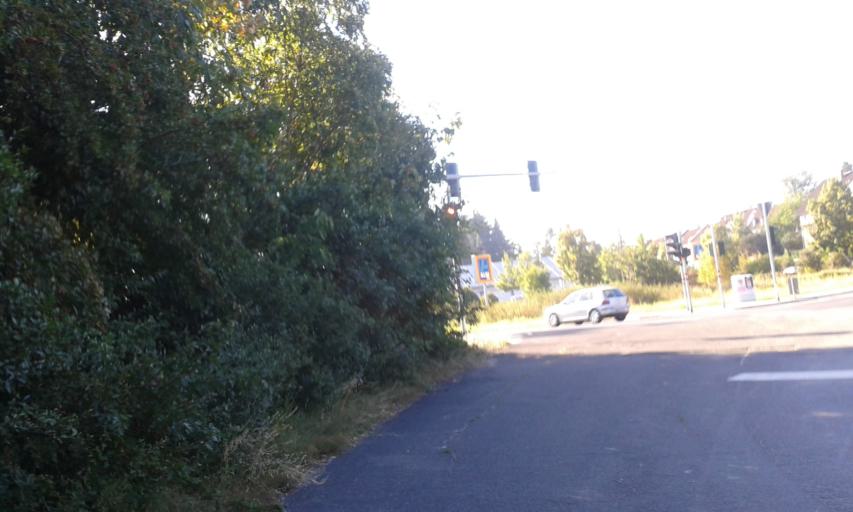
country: DE
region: Bavaria
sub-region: Upper Franconia
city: Bischberg
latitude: 49.9152
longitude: 10.8233
